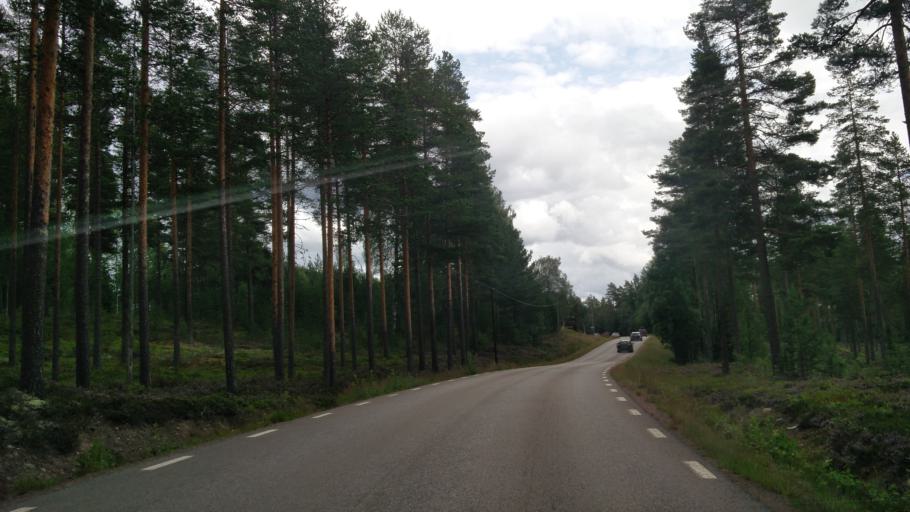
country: NO
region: Hedmark
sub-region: Trysil
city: Innbygda
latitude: 61.1765
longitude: 12.8637
